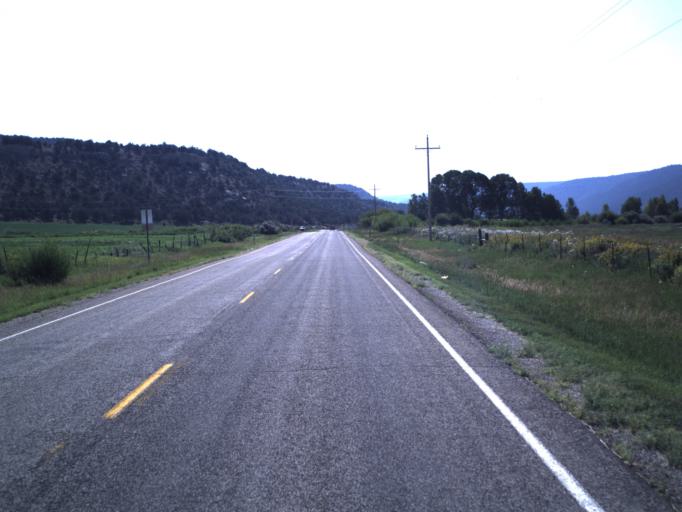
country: US
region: Utah
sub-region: Duchesne County
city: Duchesne
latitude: 40.3346
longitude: -110.6779
